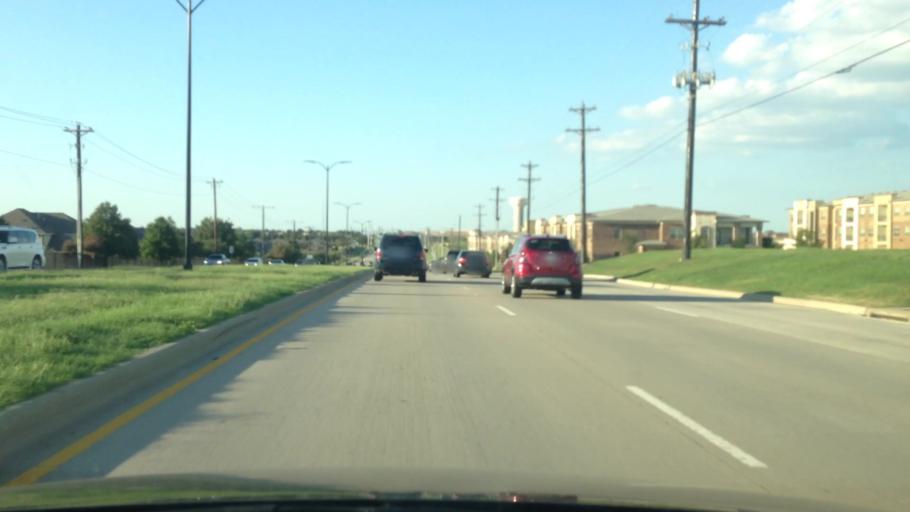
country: US
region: Texas
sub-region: Denton County
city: The Colony
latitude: 33.1294
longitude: -96.8909
